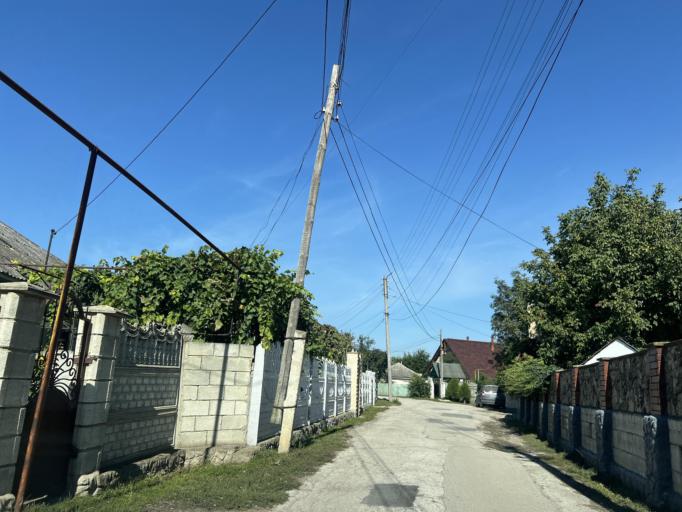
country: RO
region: Iasi
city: Ungheni-Prut
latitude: 47.1937
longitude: 27.7891
